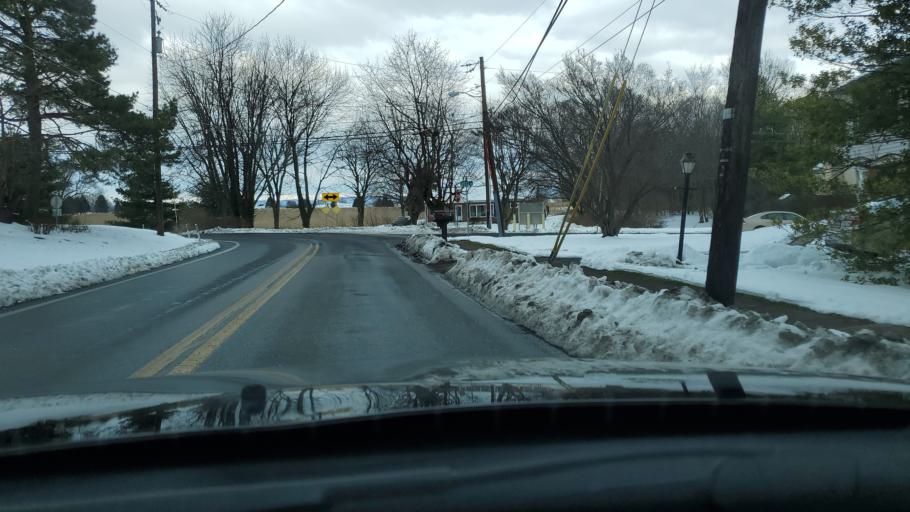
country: US
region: Pennsylvania
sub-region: Cumberland County
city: Mechanicsburg
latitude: 40.2104
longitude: -77.0320
